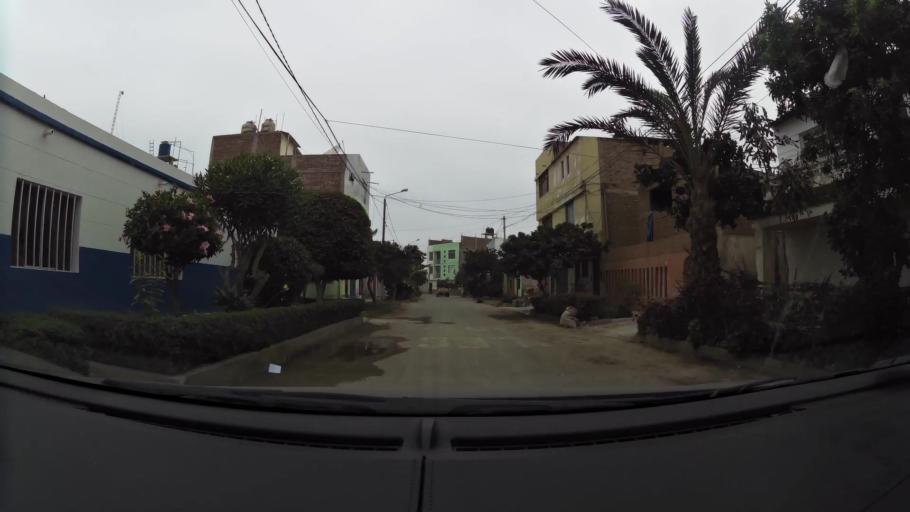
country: PE
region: La Libertad
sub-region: Provincia de Trujillo
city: Buenos Aires
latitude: -8.1436
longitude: -79.0507
